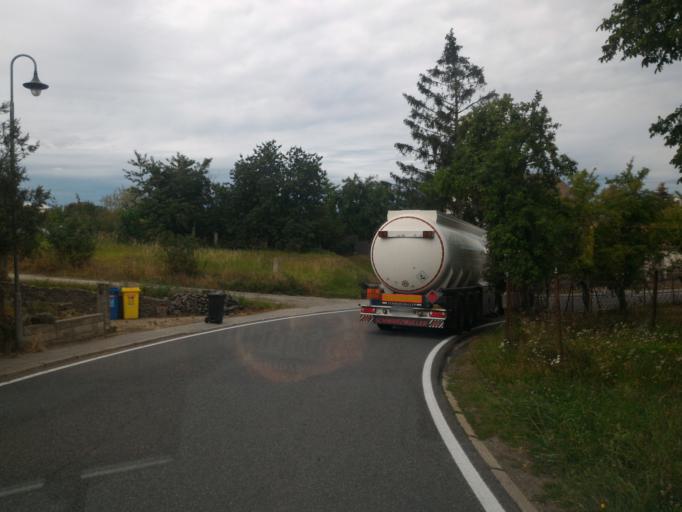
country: CZ
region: Vysocina
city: Zeletava
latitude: 49.1409
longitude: 15.5619
